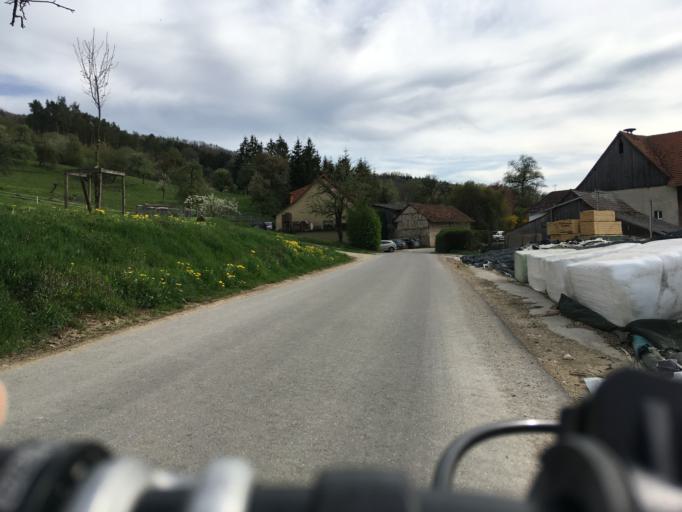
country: DE
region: Baden-Wuerttemberg
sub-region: Freiburg Region
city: Neuhausen
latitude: 47.8047
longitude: 8.7410
